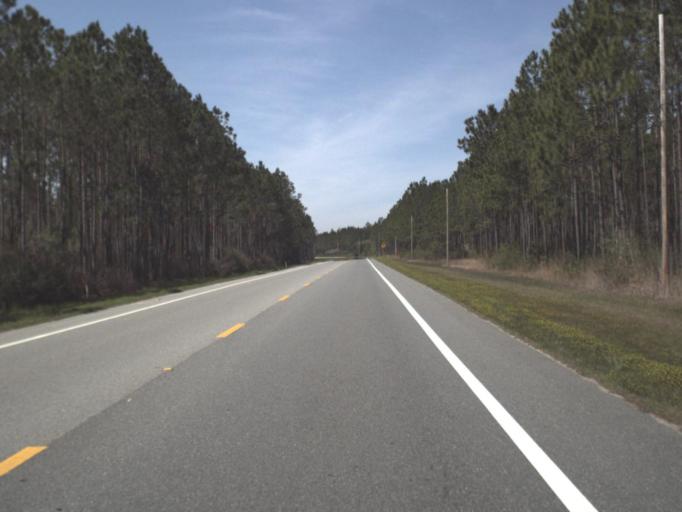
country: US
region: Florida
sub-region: Bay County
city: Lynn Haven
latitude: 30.3281
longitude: -85.7136
